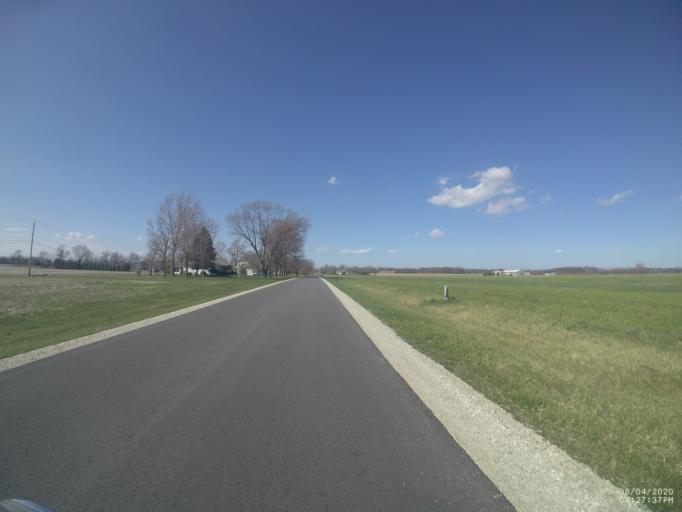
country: US
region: Ohio
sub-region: Sandusky County
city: Stony Prairie
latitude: 41.3276
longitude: -83.2020
